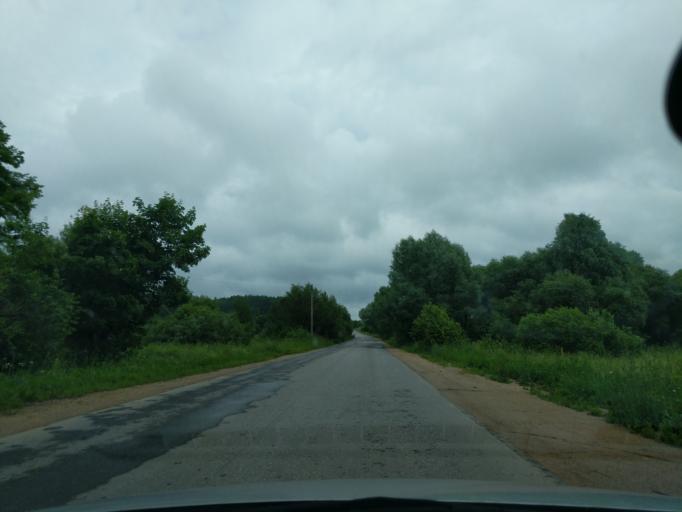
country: RU
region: Kaluga
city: Myatlevo
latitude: 54.8317
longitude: 35.6441
